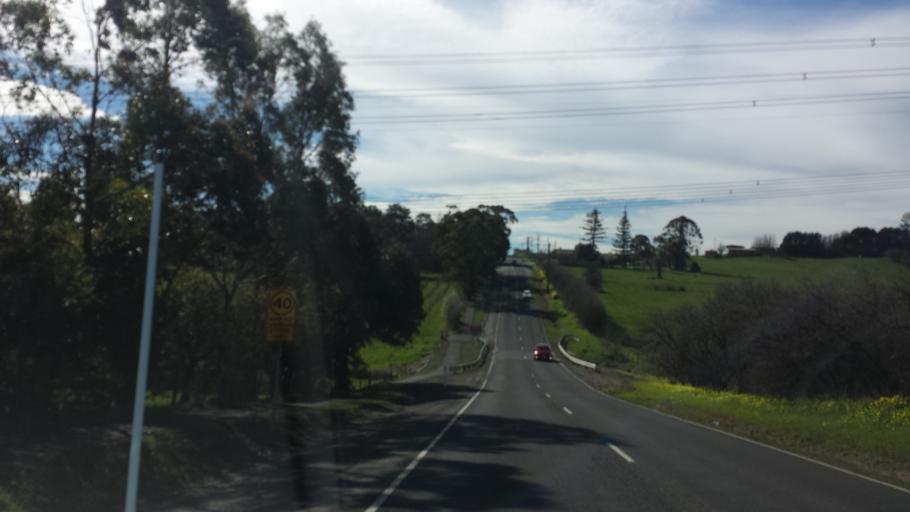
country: AU
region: Victoria
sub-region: Nillumbik
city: Research
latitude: -37.6945
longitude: 145.2150
